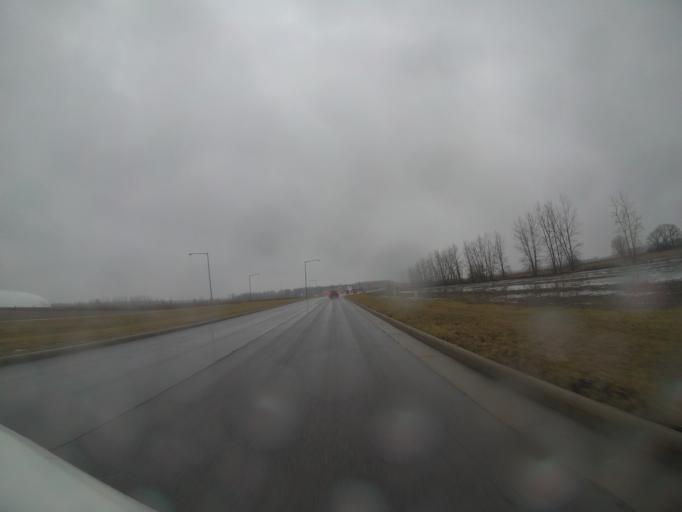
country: US
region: Ohio
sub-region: Wood County
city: Perrysburg
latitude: 41.5609
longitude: -83.5790
